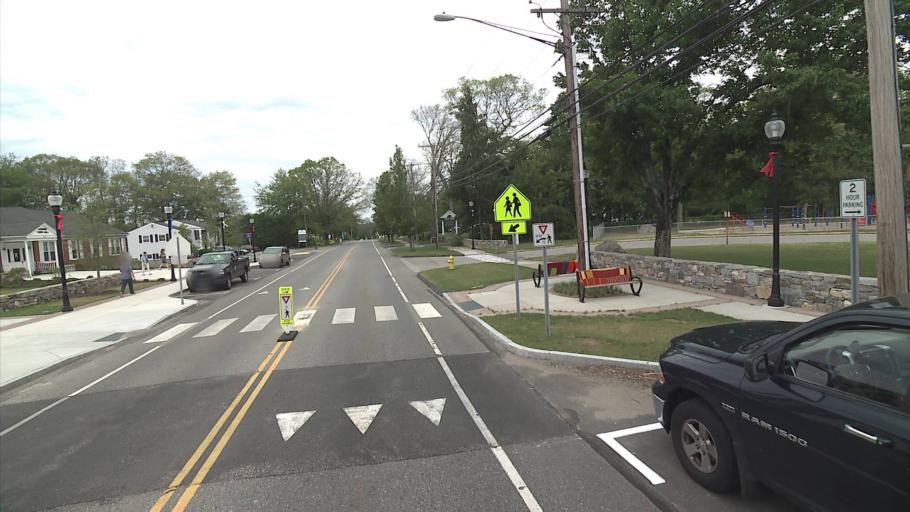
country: US
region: Connecticut
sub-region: New London County
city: Ledyard Center
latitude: 41.4423
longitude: -72.0170
